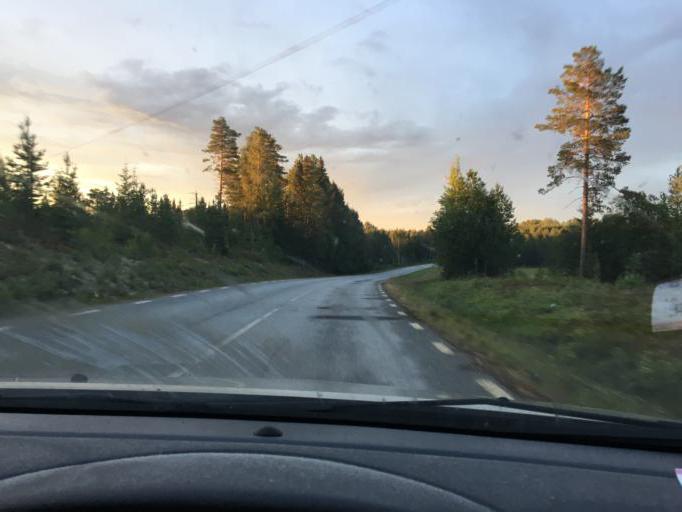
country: SE
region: Norrbotten
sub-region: Kalix Kommun
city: Toere
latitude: 66.0671
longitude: 22.6829
